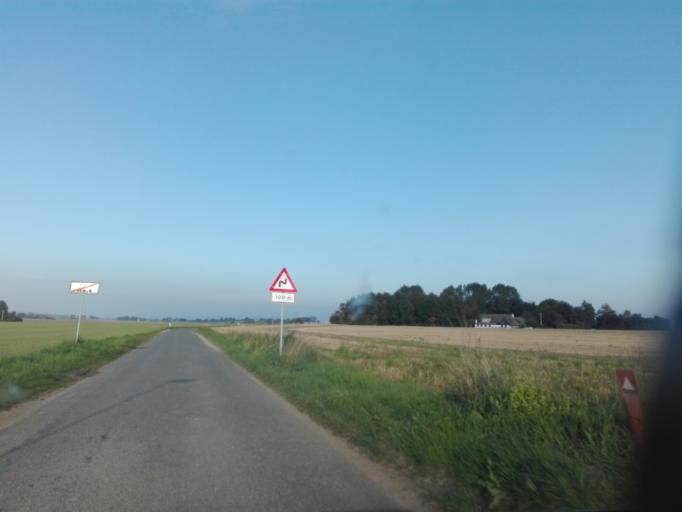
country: DK
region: Central Jutland
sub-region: Odder Kommune
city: Odder
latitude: 55.9765
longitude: 10.1956
